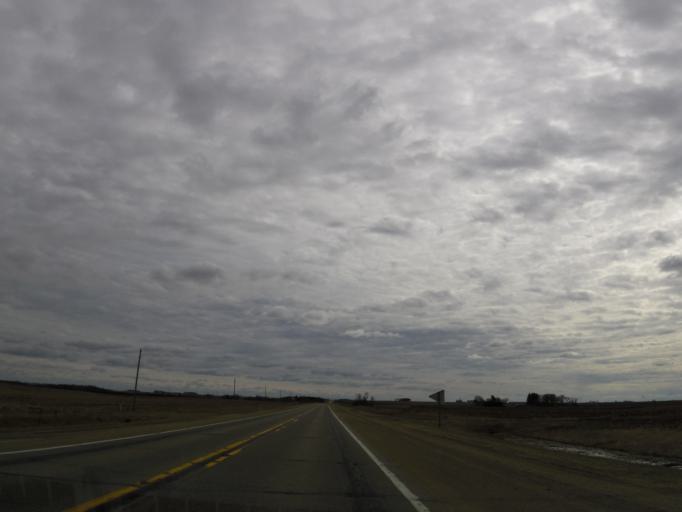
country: US
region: Iowa
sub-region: Howard County
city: Cresco
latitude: 43.4041
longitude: -92.2985
